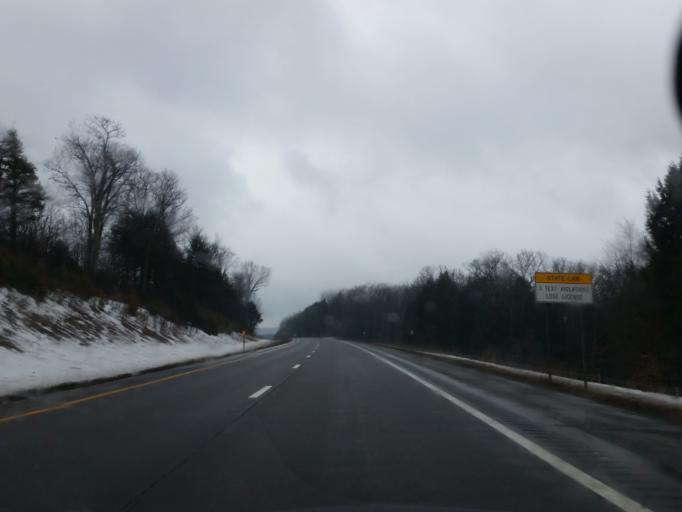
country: US
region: New York
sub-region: Chenango County
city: Lakeview
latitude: 42.3678
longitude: -75.9952
